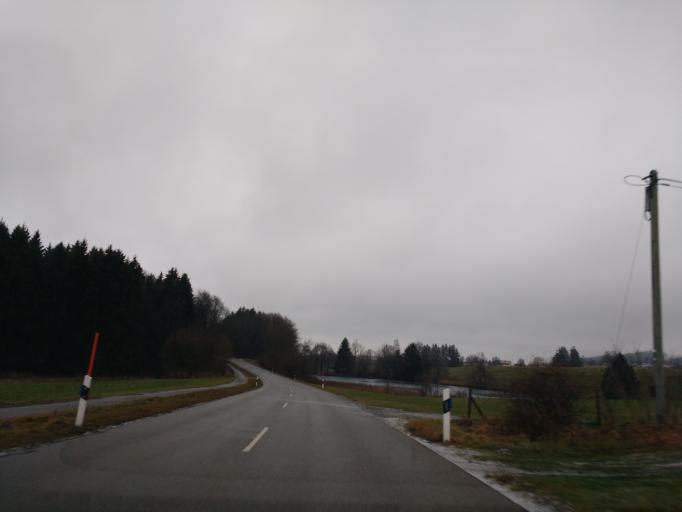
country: DE
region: Bavaria
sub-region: Swabia
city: Neuburg
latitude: 47.7690
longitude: 10.3701
